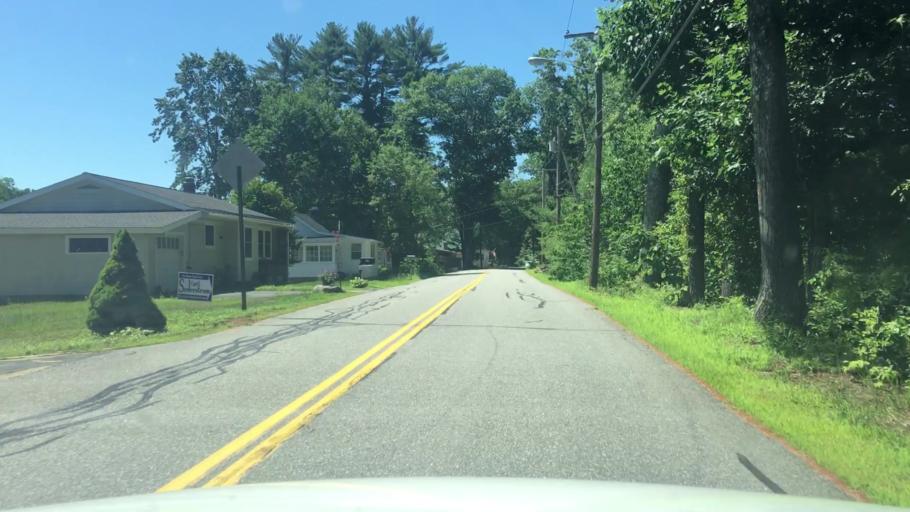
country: US
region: New Hampshire
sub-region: Merrimack County
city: Boscawen
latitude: 43.2604
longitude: -71.6219
